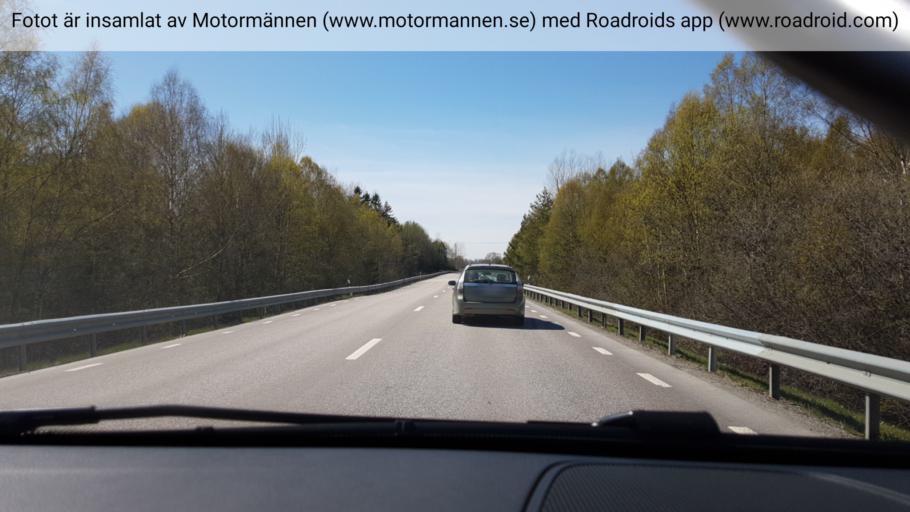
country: SE
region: Stockholm
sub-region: Nynashamns Kommun
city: Osmo
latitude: 58.9838
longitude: 17.8632
